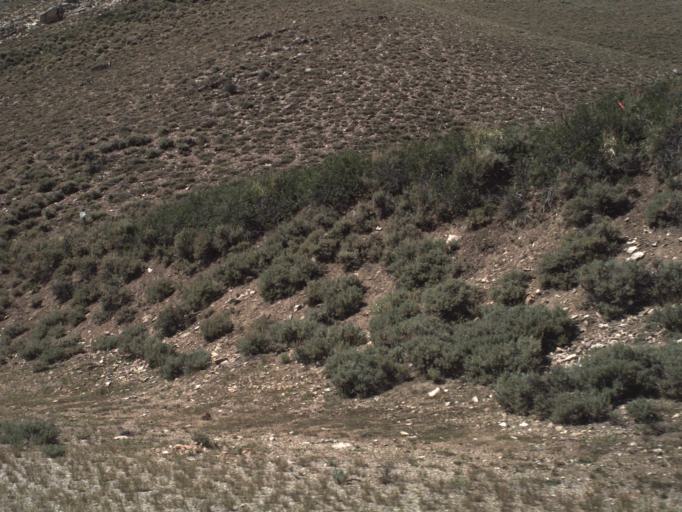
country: US
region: Utah
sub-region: Rich County
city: Randolph
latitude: 41.4833
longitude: -111.3912
